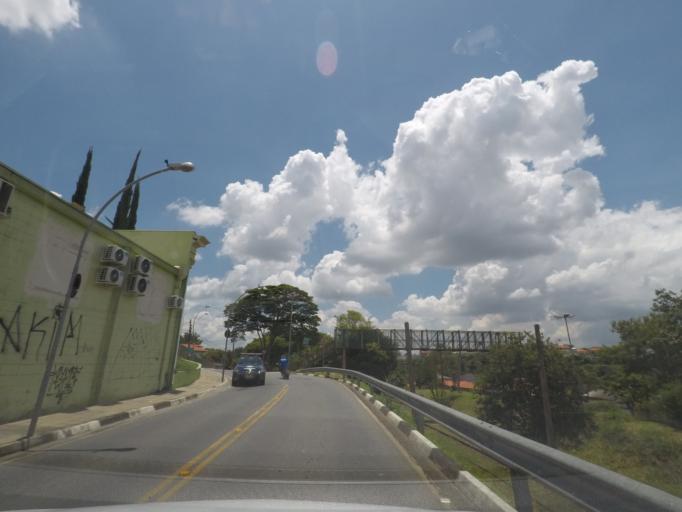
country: BR
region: Sao Paulo
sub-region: Vinhedo
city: Vinhedo
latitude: -23.0271
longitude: -46.9738
